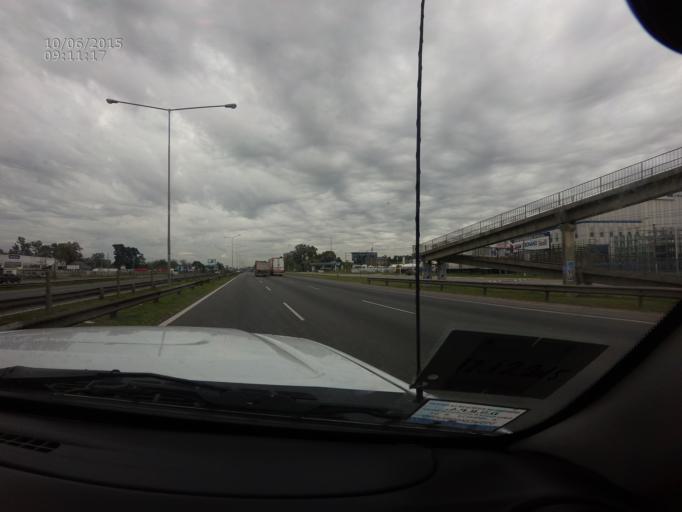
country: AR
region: Buenos Aires
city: Belen de Escobar
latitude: -34.3635
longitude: -58.7872
